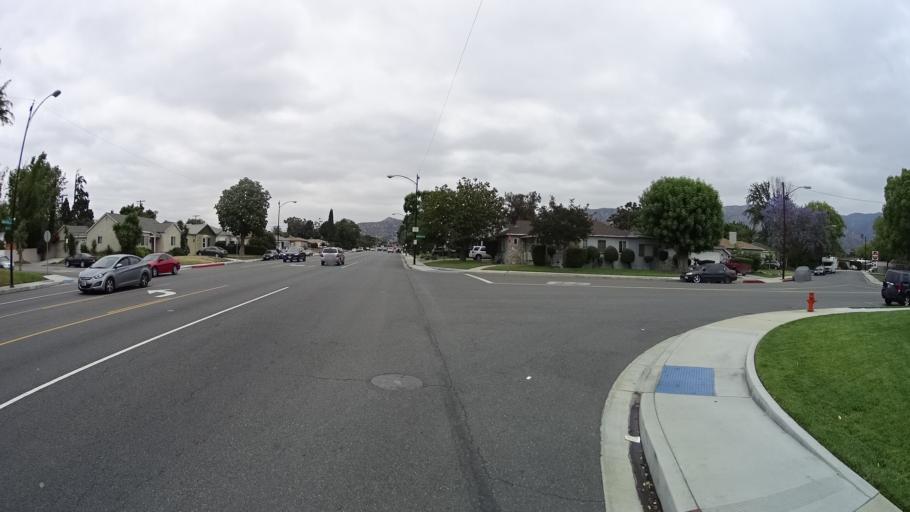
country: US
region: California
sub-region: Los Angeles County
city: Burbank
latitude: 34.1861
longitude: -118.3383
